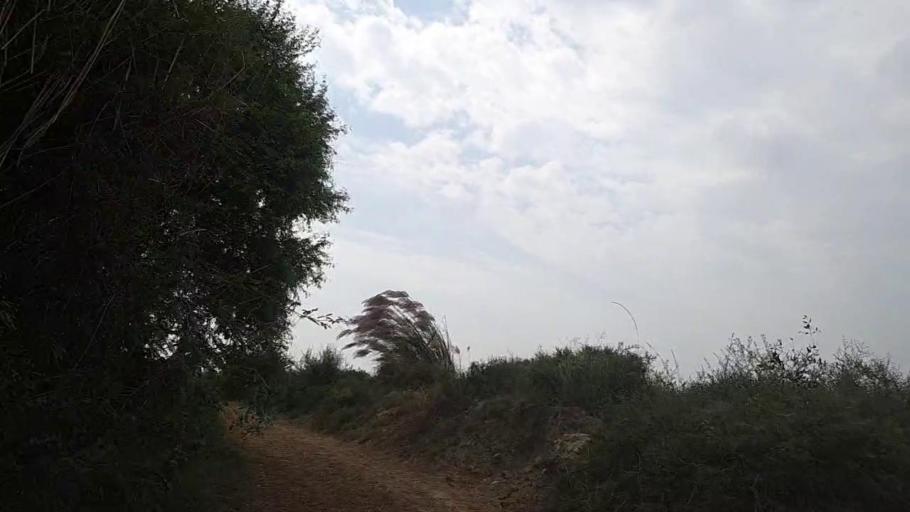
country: PK
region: Sindh
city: Mirpur Batoro
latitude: 24.6141
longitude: 68.1350
